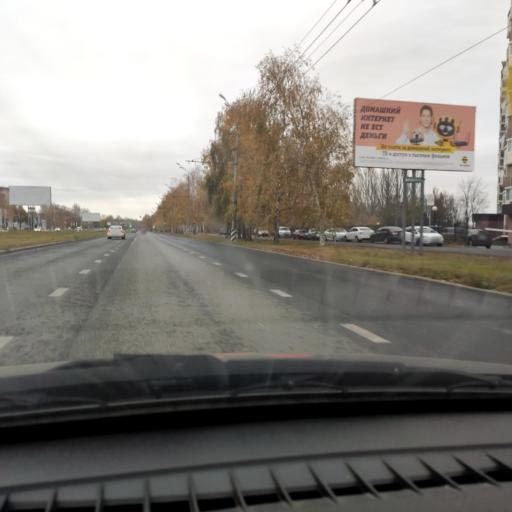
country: RU
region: Samara
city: Tol'yatti
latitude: 53.5032
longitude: 49.2595
